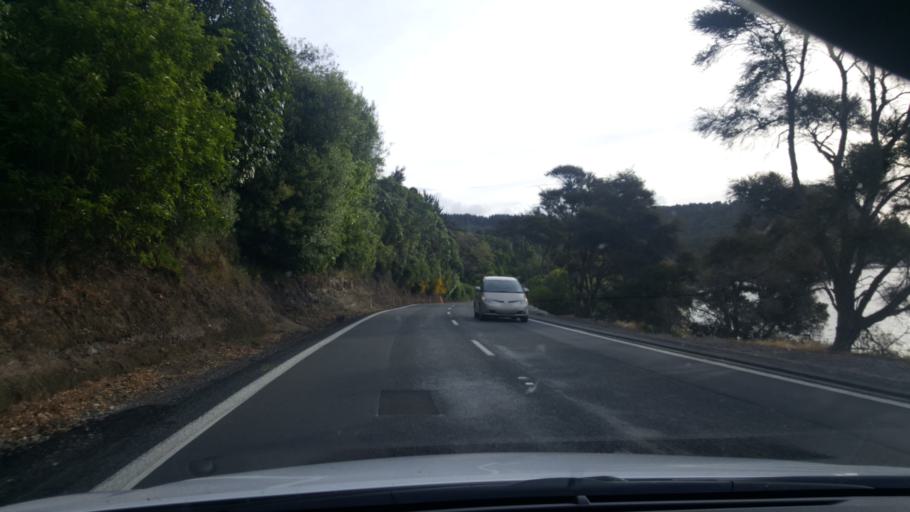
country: NZ
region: Waikato
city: Turangi
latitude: -38.8843
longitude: 175.9659
